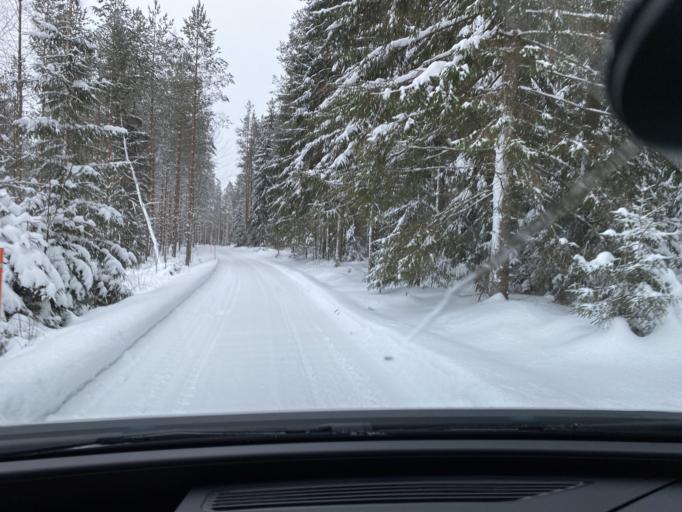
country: FI
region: Pirkanmaa
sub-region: Lounais-Pirkanmaa
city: Punkalaidun
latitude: 61.1348
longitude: 23.0943
